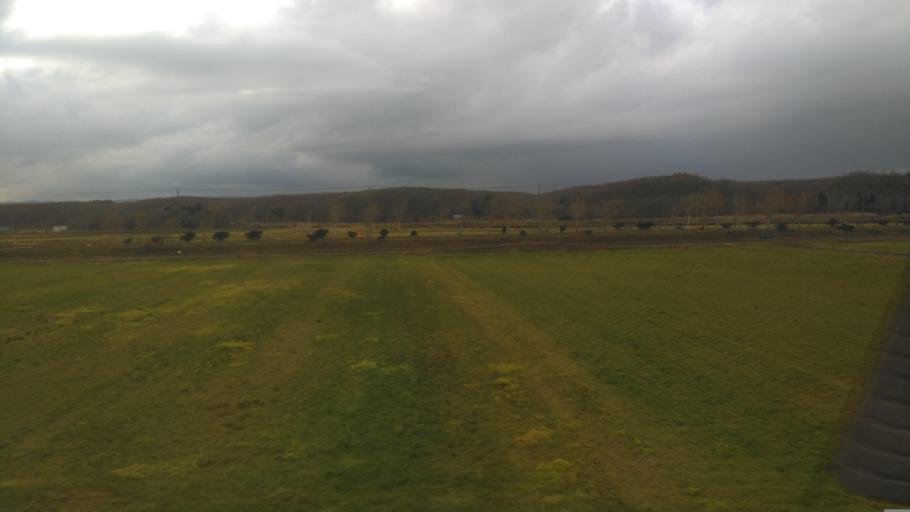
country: JP
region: Hokkaido
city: Kitahiroshima
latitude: 42.9382
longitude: 141.5722
